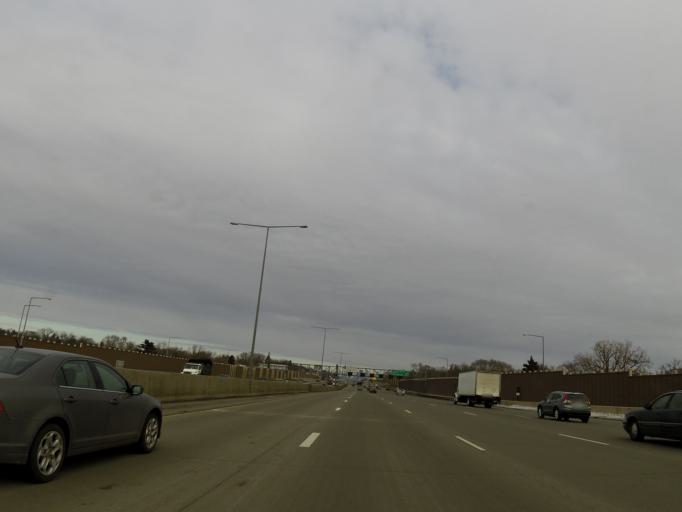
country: US
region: Minnesota
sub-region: Hennepin County
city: Richfield
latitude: 44.8949
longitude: -93.2749
